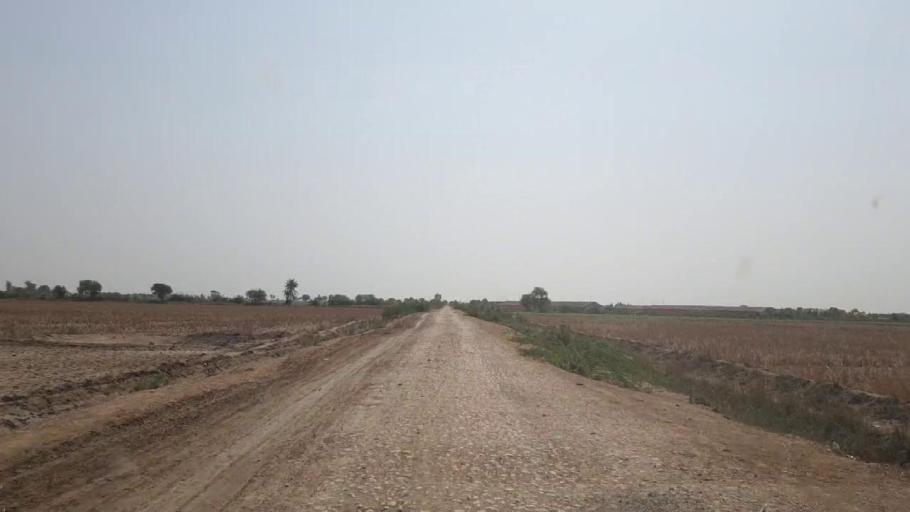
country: PK
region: Sindh
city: Jati
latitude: 24.4276
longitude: 68.5524
